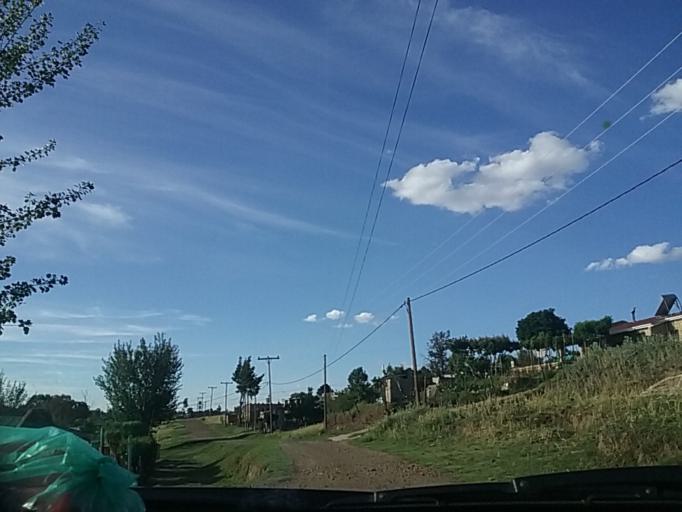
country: LS
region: Berea
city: Teyateyaneng
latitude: -29.1508
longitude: 27.7385
